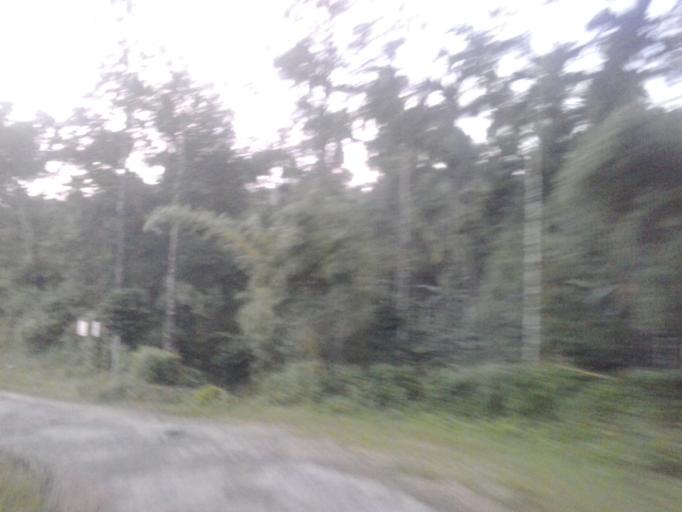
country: IN
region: Karnataka
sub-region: Chikmagalur
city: Mudigere
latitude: 13.0108
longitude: 75.6698
